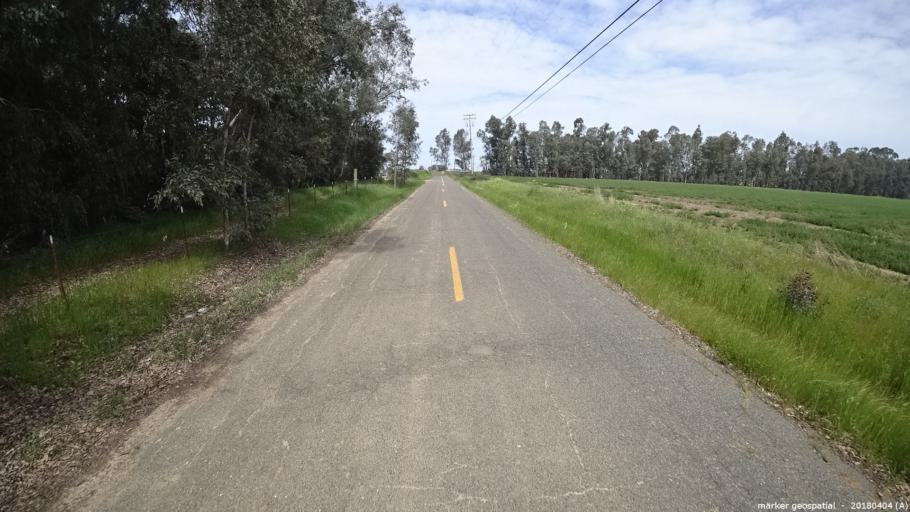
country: US
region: California
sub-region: Sacramento County
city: Herald
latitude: 38.2757
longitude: -121.2543
